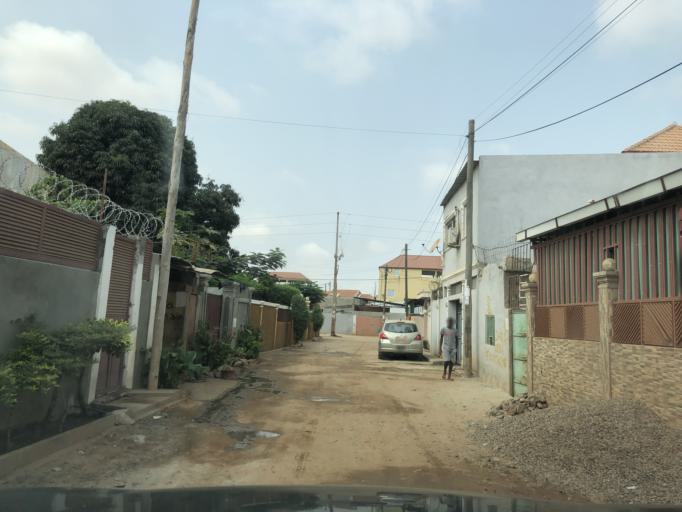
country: AO
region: Luanda
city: Luanda
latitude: -8.9174
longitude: 13.1715
